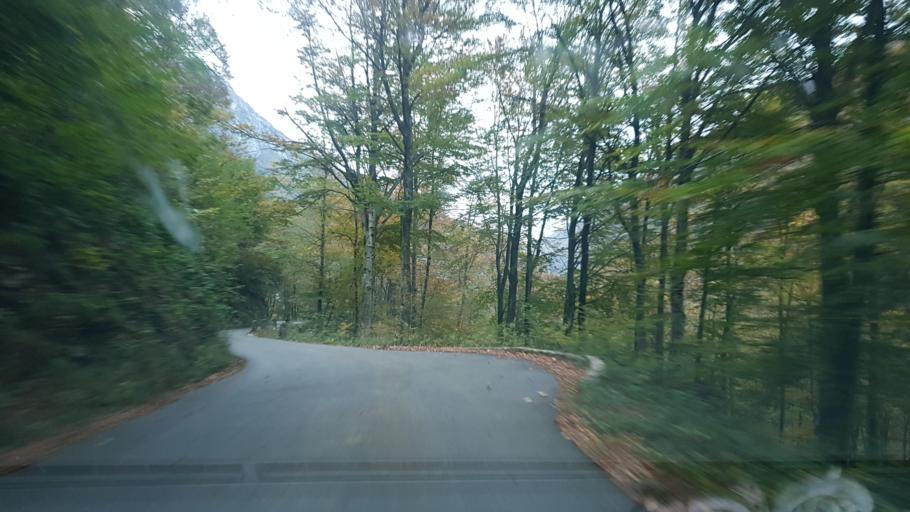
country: IT
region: Friuli Venezia Giulia
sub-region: Provincia di Udine
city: Preone
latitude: 46.3417
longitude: 12.8894
